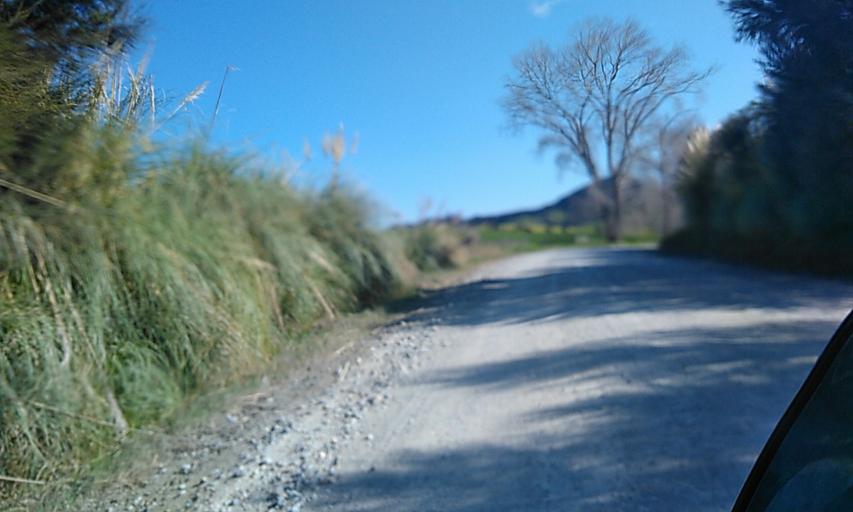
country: NZ
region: Gisborne
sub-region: Gisborne District
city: Gisborne
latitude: -38.4923
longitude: 178.0583
